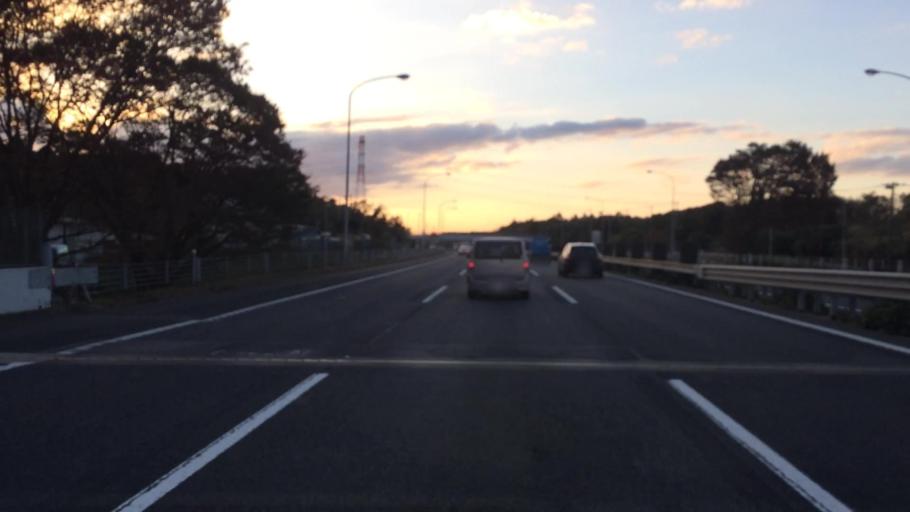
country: JP
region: Chiba
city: Yotsukaido
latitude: 35.6844
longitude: 140.1788
